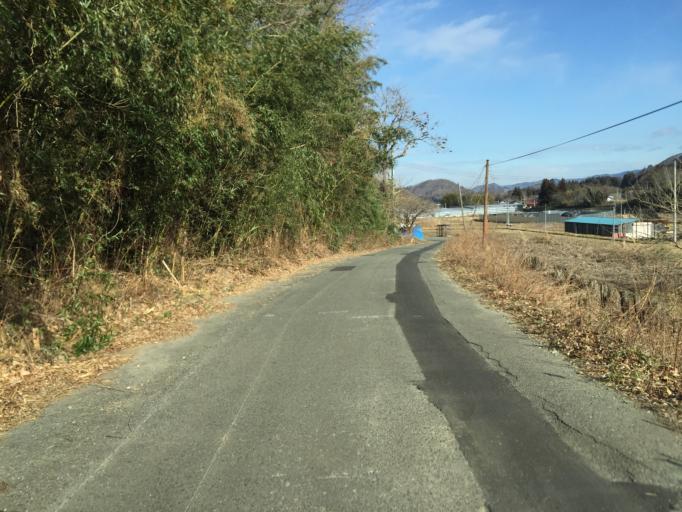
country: JP
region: Fukushima
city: Hobaramachi
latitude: 37.7455
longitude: 140.5626
